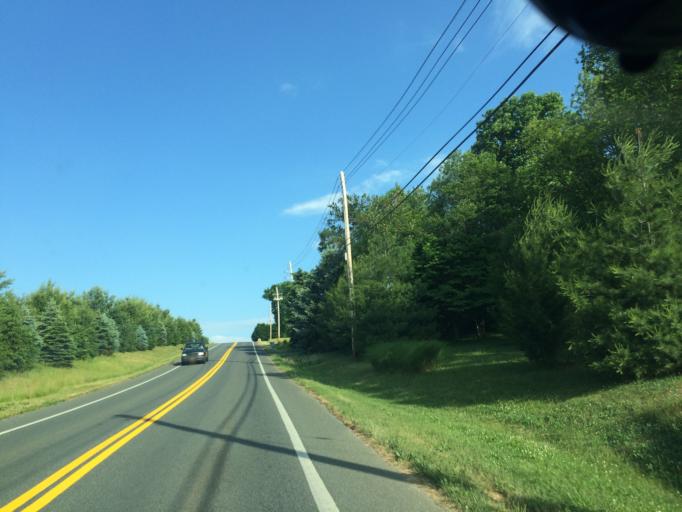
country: US
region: Maryland
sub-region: Carroll County
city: Sykesville
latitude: 39.3882
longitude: -77.0150
